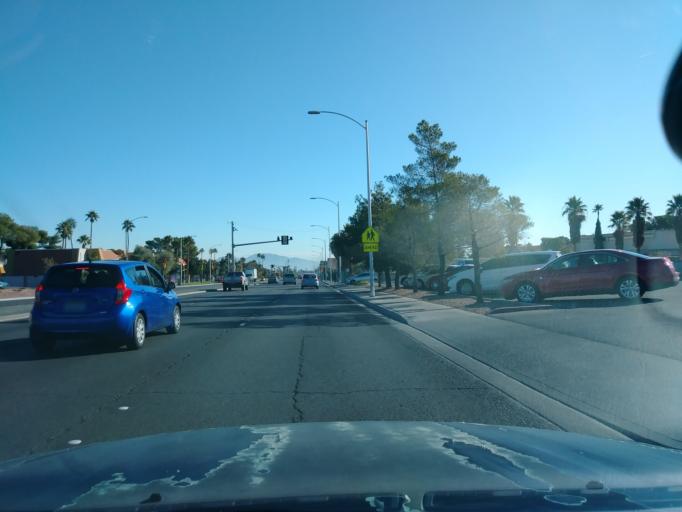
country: US
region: Nevada
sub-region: Clark County
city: Spring Valley
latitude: 36.1590
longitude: -115.2412
